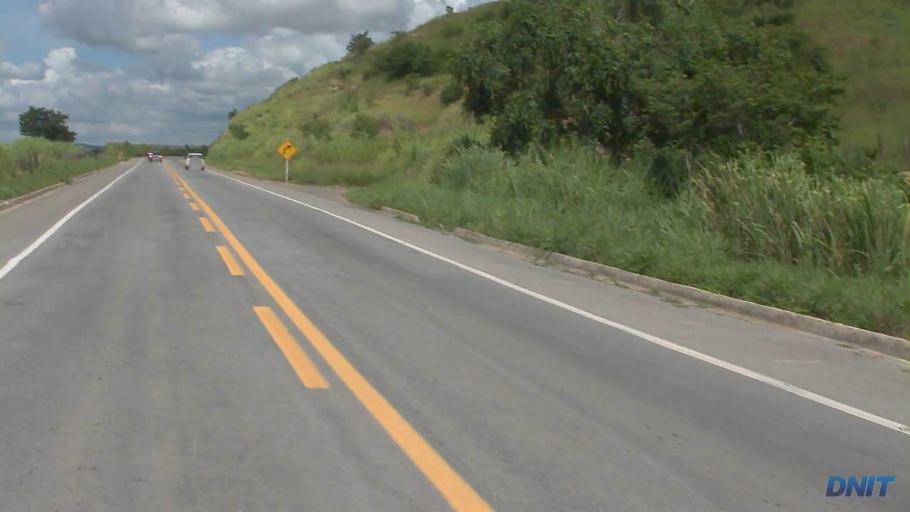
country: BR
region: Minas Gerais
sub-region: Governador Valadares
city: Governador Valadares
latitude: -18.9722
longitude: -42.0947
